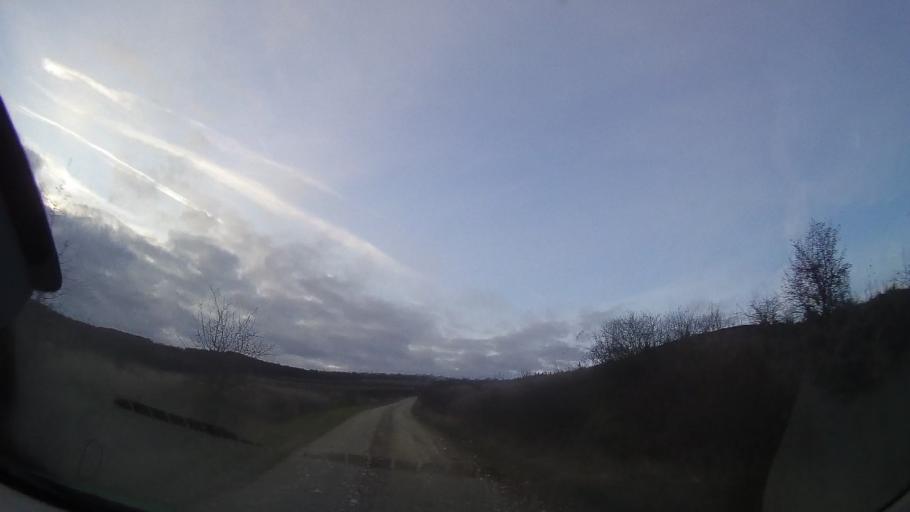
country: RO
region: Cluj
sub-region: Comuna Palatca
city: Palatca
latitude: 46.8574
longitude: 24.0332
